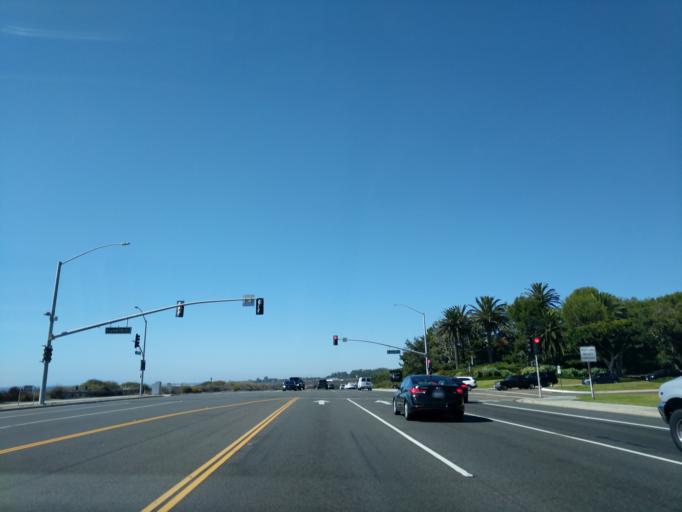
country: US
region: California
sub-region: Orange County
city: San Joaquin Hills
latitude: 33.5708
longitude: -117.8354
